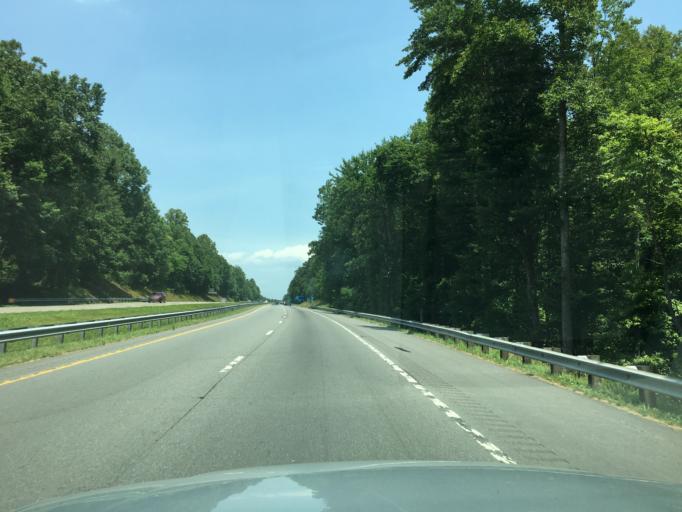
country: US
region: North Carolina
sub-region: McDowell County
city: West Marion
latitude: 35.6366
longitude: -81.9934
